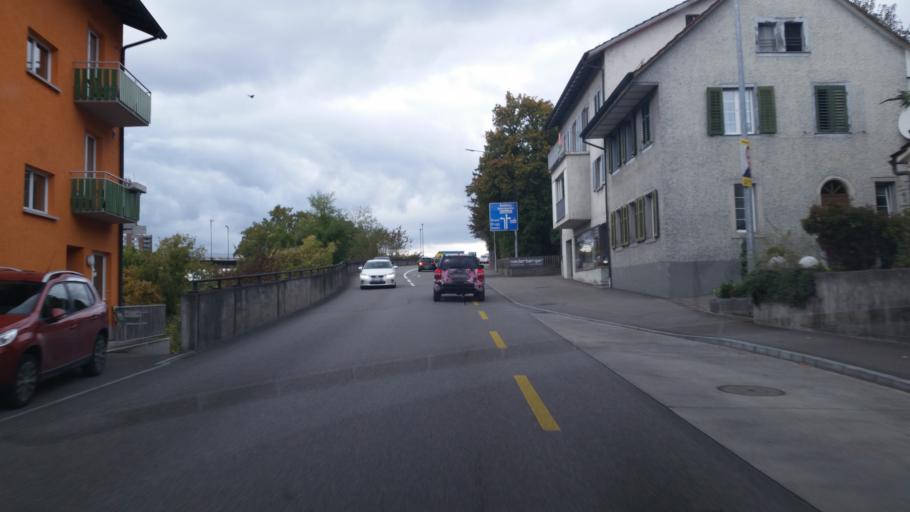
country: CH
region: Aargau
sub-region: Bezirk Baden
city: Obersiggenthal
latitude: 47.4836
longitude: 8.3021
